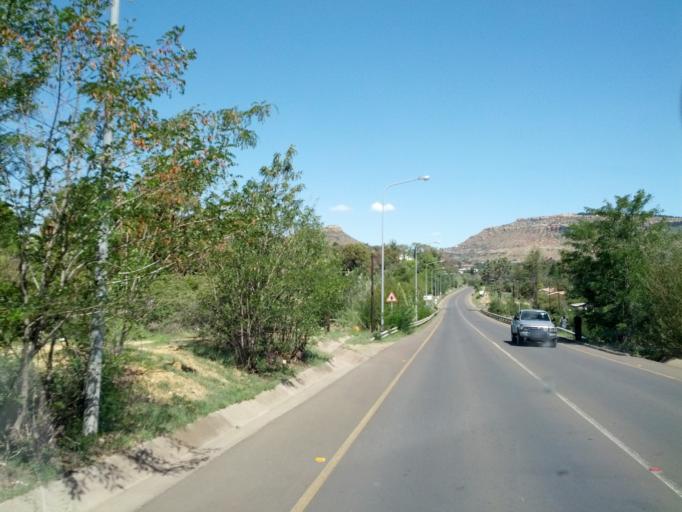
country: LS
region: Maseru
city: Maseru
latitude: -29.3114
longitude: 27.4677
